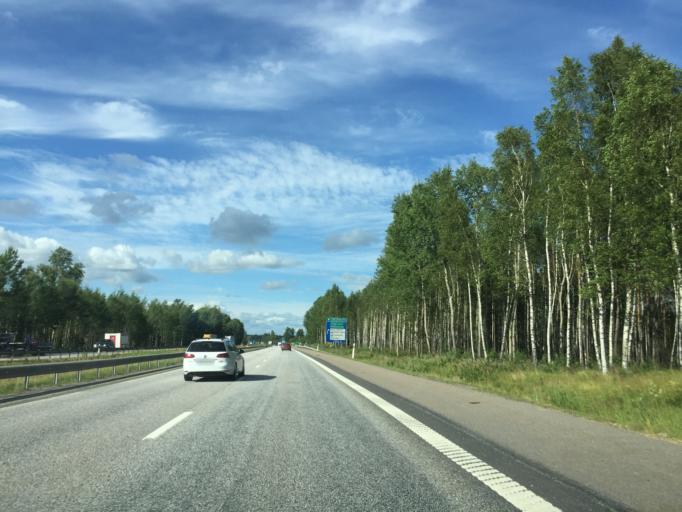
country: SE
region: OErebro
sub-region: Orebro Kommun
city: Orebro
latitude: 59.2254
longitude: 15.1393
